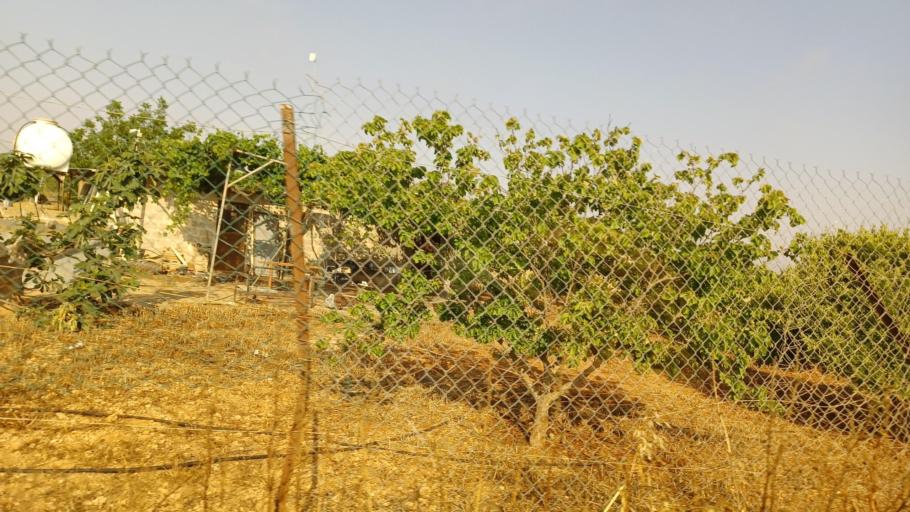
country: CY
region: Ammochostos
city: Avgorou
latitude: 35.0492
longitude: 33.8217
